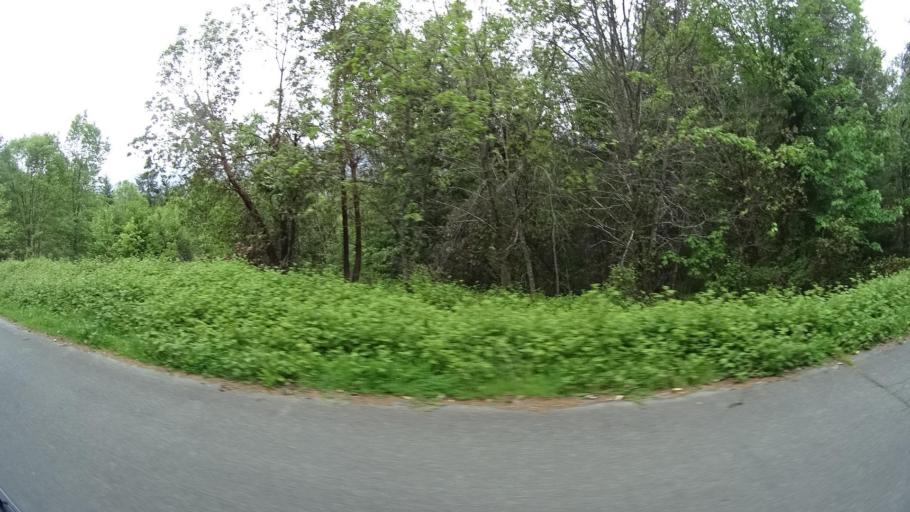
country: US
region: California
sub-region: Humboldt County
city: Willow Creek
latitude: 41.1171
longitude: -123.7204
